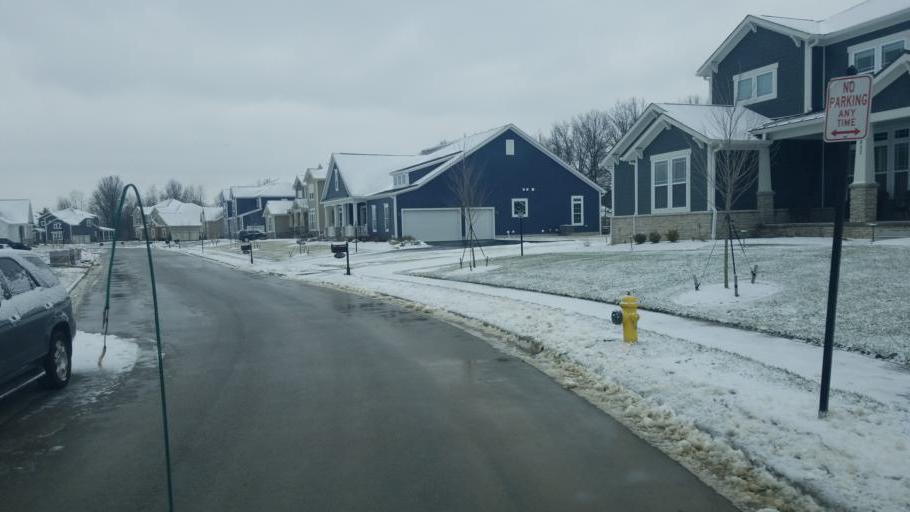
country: US
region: Ohio
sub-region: Franklin County
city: New Albany
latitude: 40.0448
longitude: -82.7884
